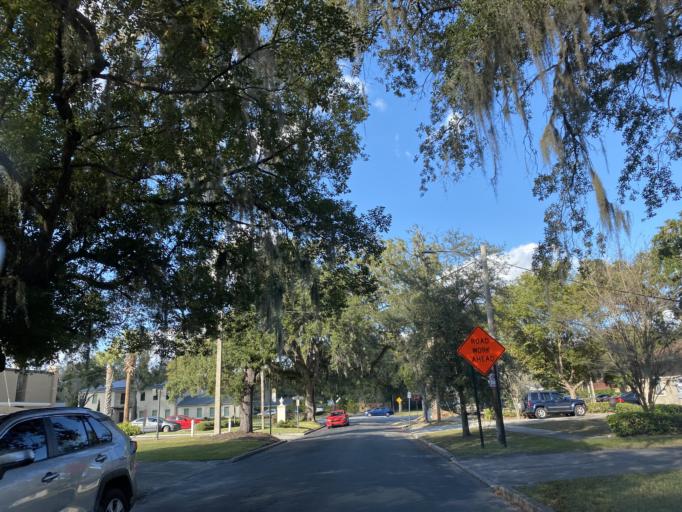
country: US
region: Florida
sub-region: Orange County
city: Orlando
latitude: 28.5522
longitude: -81.4016
